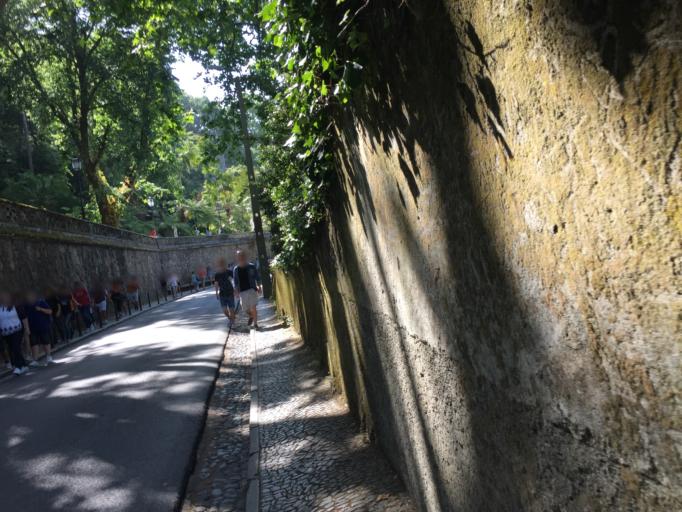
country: PT
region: Lisbon
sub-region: Sintra
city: Sintra
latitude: 38.7954
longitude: -9.3948
